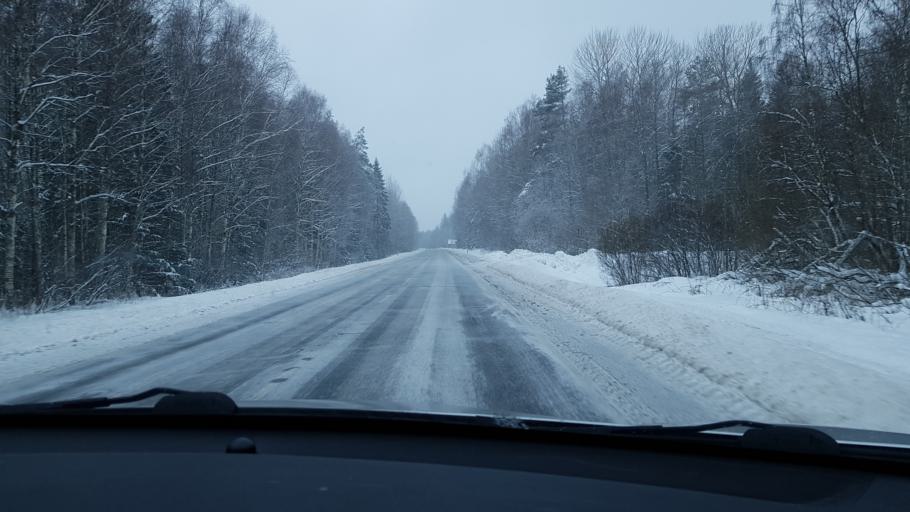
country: EE
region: Jaervamaa
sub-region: Tueri vald
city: Sarevere
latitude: 58.7466
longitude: 25.3129
